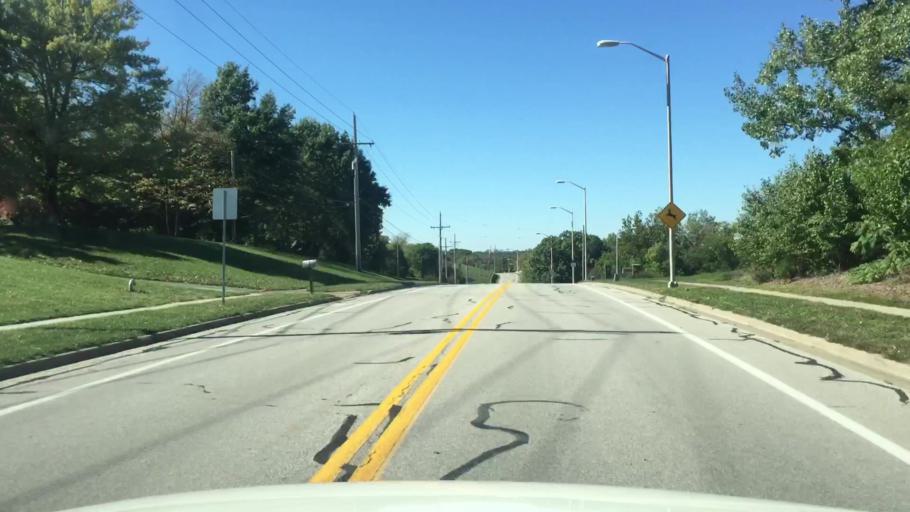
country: US
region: Kansas
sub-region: Johnson County
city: Shawnee
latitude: 39.0367
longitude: -94.7431
